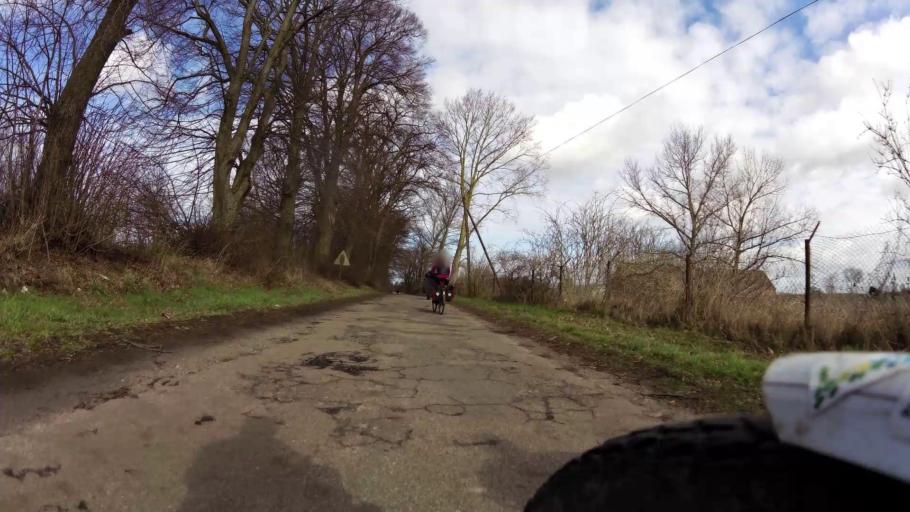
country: PL
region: West Pomeranian Voivodeship
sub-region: Powiat kamienski
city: Kamien Pomorski
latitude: 53.9916
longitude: 14.7686
